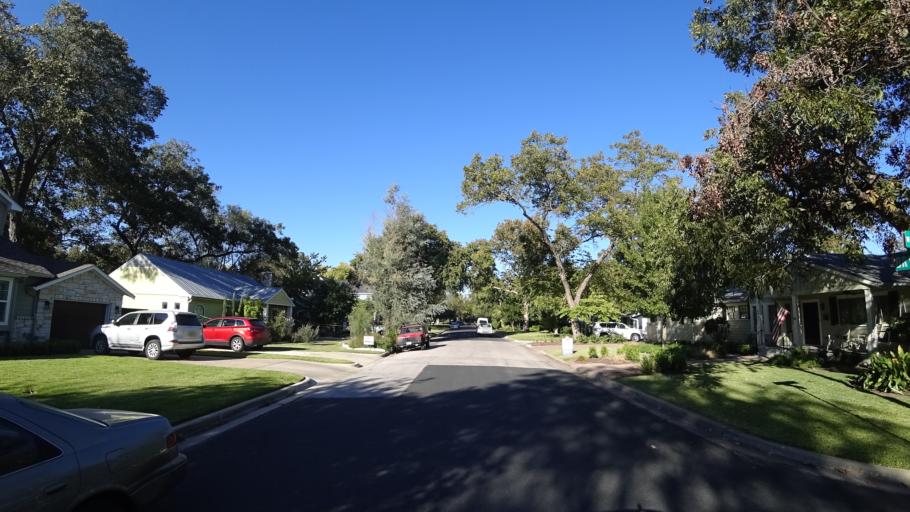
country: US
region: Texas
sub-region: Travis County
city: Austin
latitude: 30.3057
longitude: -97.7538
